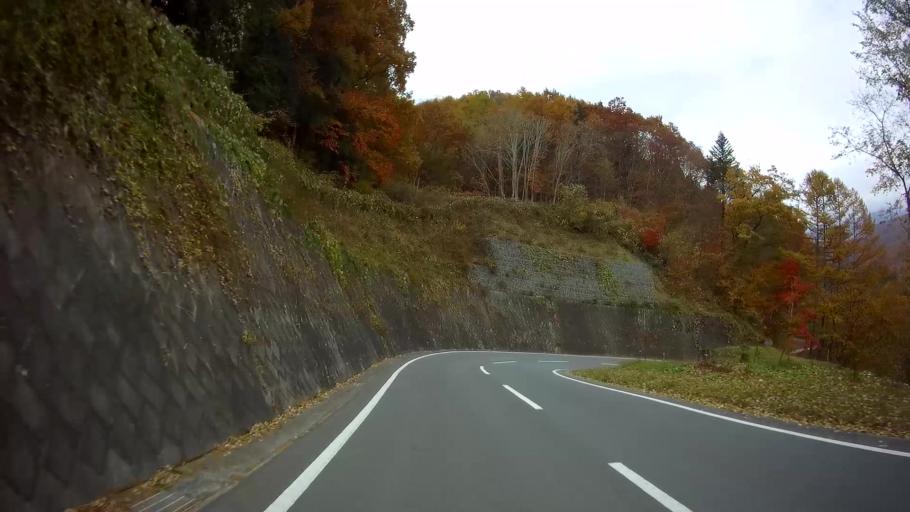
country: JP
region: Gunma
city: Nakanojomachi
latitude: 36.6522
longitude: 138.6522
